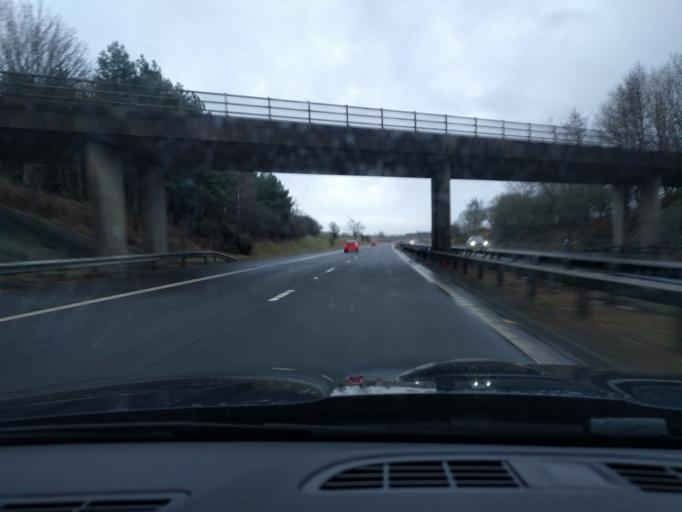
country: GB
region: Scotland
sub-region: West Lothian
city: Broxburn
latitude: 55.9755
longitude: -3.4739
